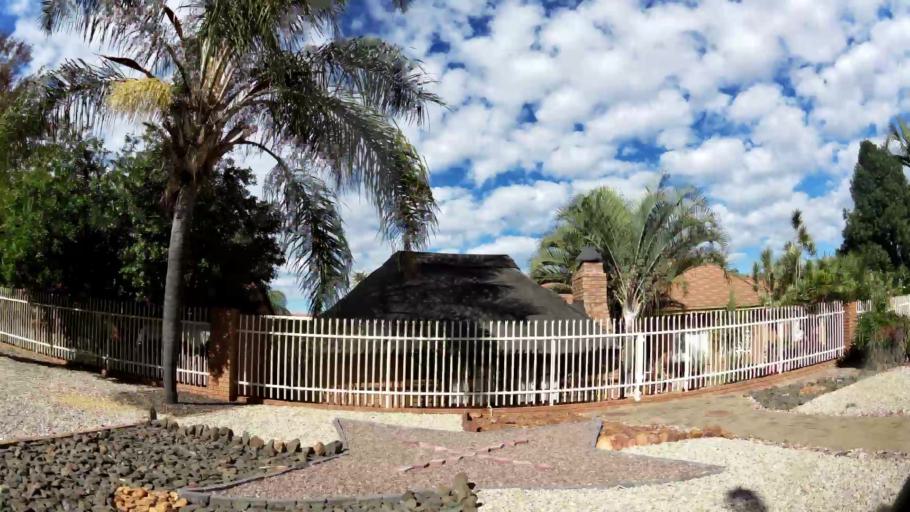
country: ZA
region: Limpopo
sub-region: Waterberg District Municipality
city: Warmbaths
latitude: -24.8735
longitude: 28.2842
